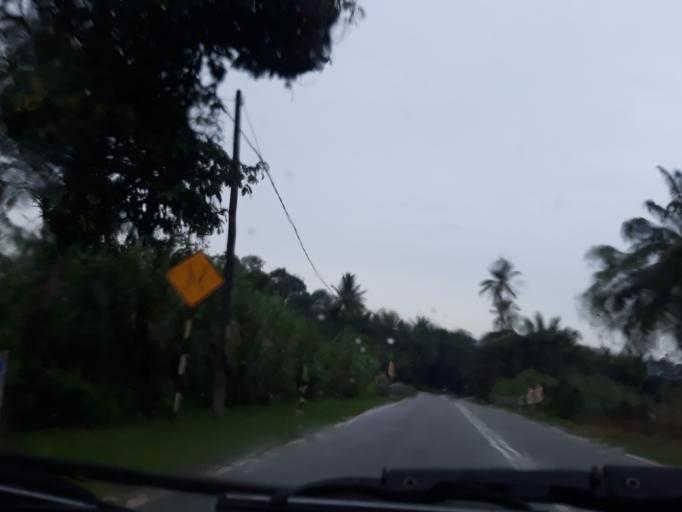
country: MY
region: Kedah
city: Kulim
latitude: 5.2374
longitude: 100.6020
